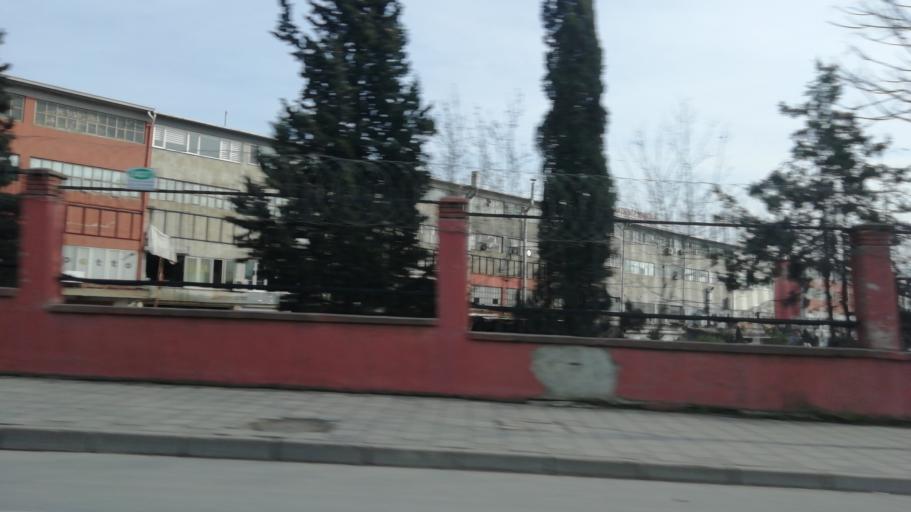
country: TR
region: Istanbul
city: Basaksehir
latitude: 41.1004
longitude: 28.7927
